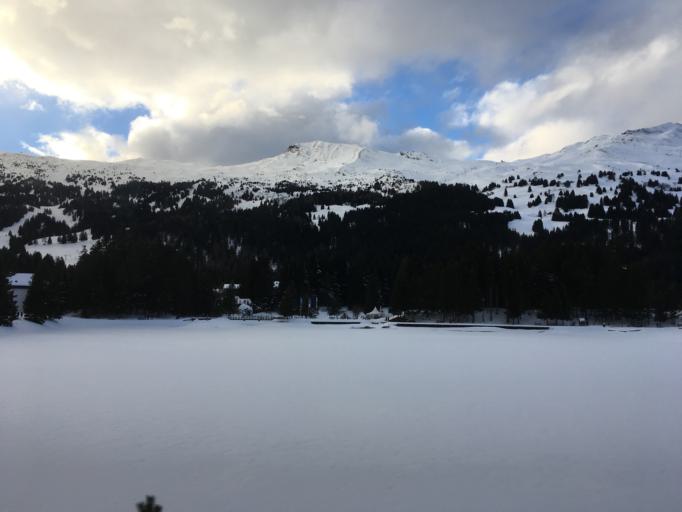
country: CH
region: Grisons
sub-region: Plessur District
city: Churwalden
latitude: 46.7356
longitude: 9.5523
